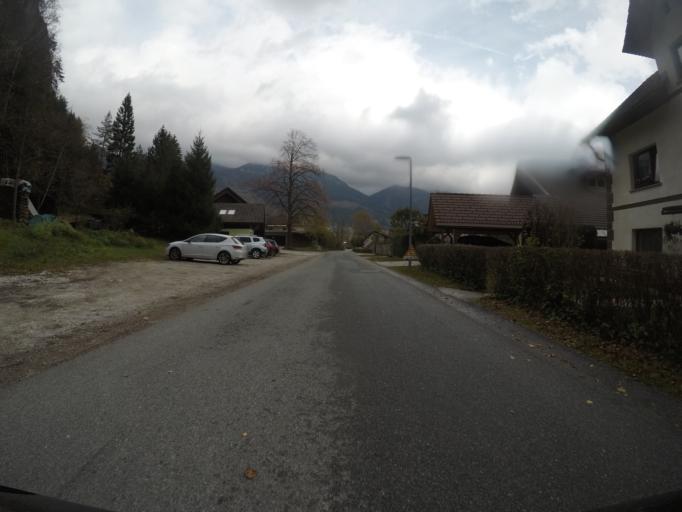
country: SI
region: Kranjska Gora
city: Mojstrana
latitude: 46.4573
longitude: 13.9345
